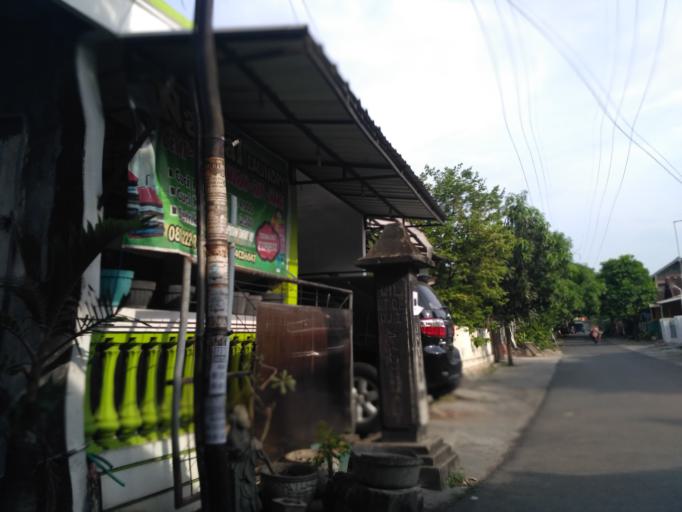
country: ID
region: Central Java
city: Semarang
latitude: -7.0150
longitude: 110.4443
